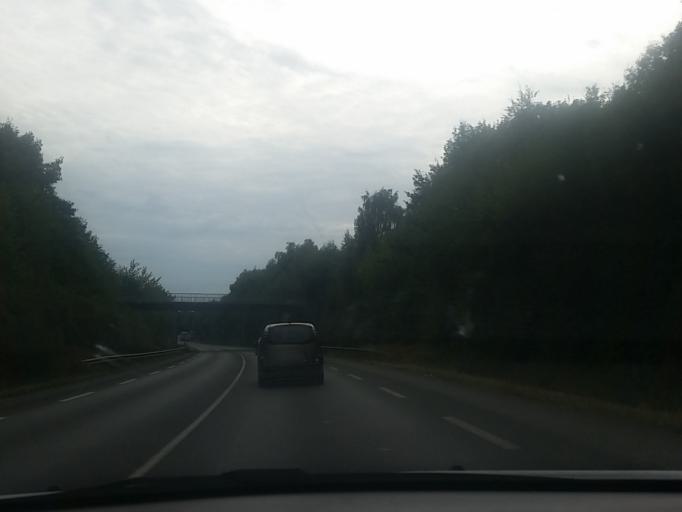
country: FR
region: Pays de la Loire
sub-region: Departement de la Vendee
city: Saint-Fulgent
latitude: 46.8631
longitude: -1.1859
